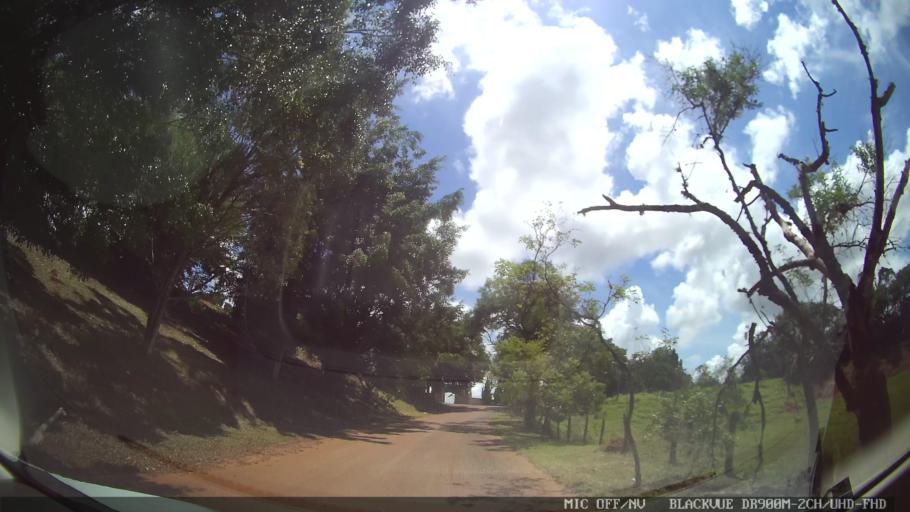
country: BR
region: Sao Paulo
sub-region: Amparo
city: Amparo
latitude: -22.8033
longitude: -46.7010
